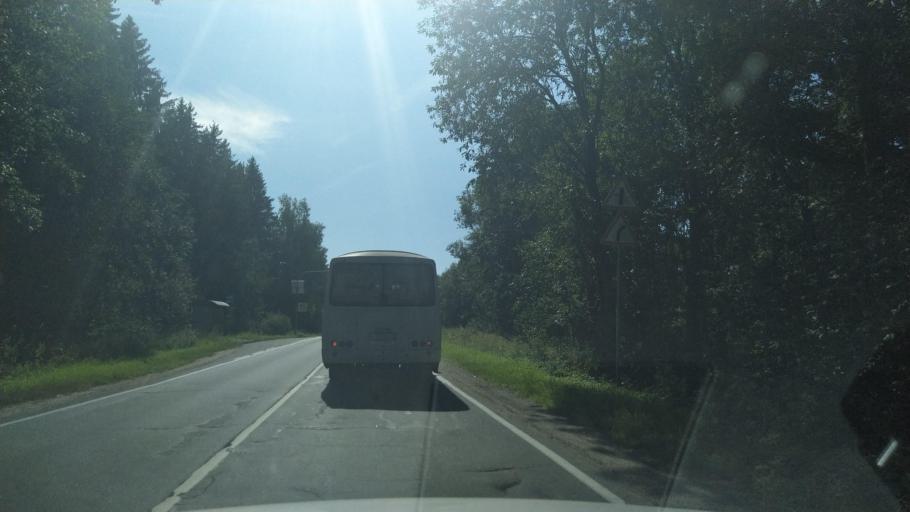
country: RU
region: Leningrad
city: Siverskiy
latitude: 59.3305
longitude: 30.0620
